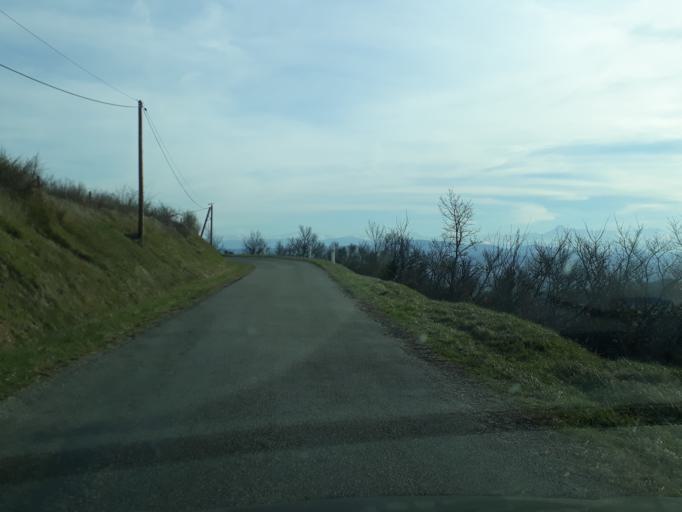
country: FR
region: Midi-Pyrenees
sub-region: Departement de la Haute-Garonne
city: Montesquieu-Volvestre
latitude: 43.1820
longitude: 1.2998
